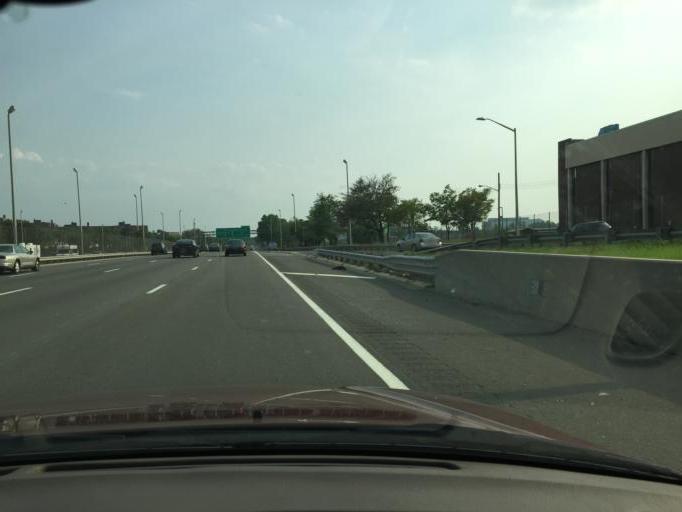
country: US
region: New York
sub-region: Nassau County
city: East Atlantic Beach
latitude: 40.7803
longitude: -73.8260
